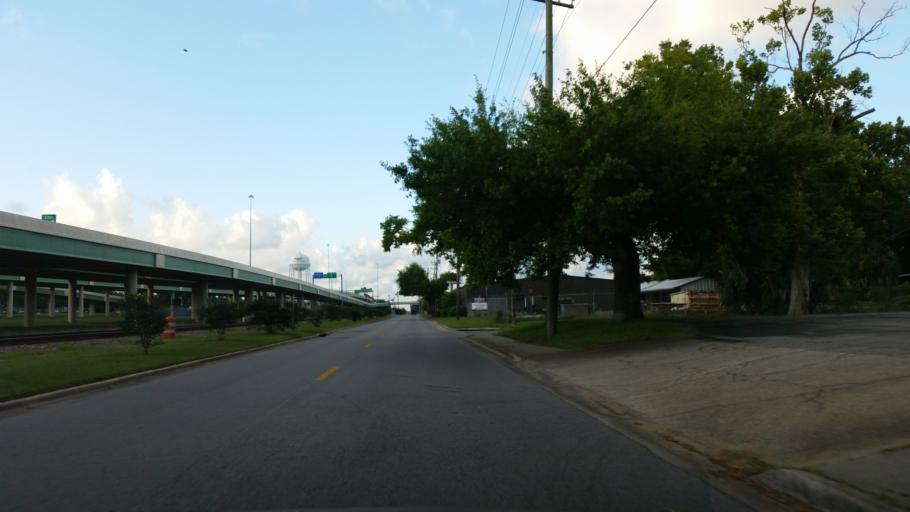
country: US
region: Florida
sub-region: Escambia County
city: Pensacola
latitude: 30.4270
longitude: -87.2160
